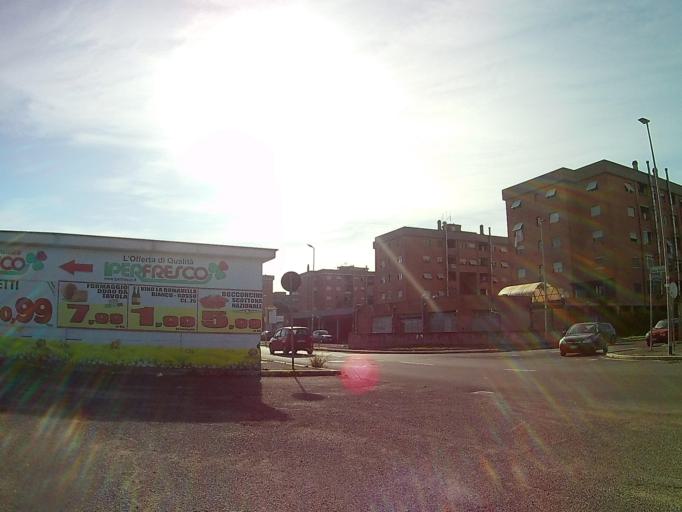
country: IT
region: Latium
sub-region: Citta metropolitana di Roma Capitale
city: Lido di Ostia
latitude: 41.7401
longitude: 12.2616
